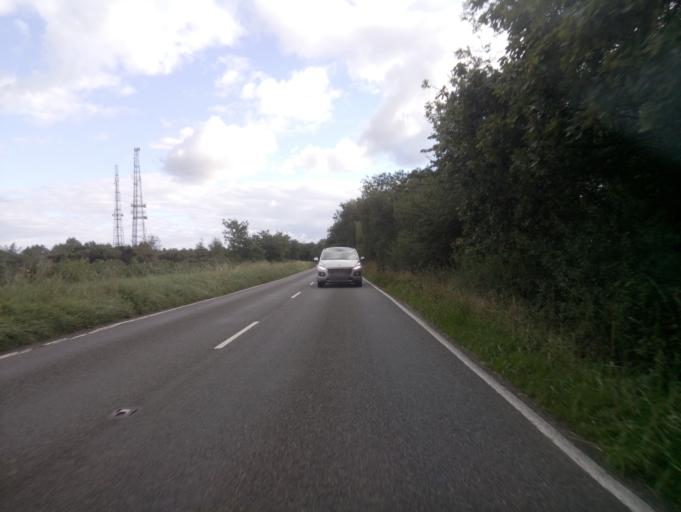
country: GB
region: England
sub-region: Devon
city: Honiton
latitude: 50.7645
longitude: -3.2133
